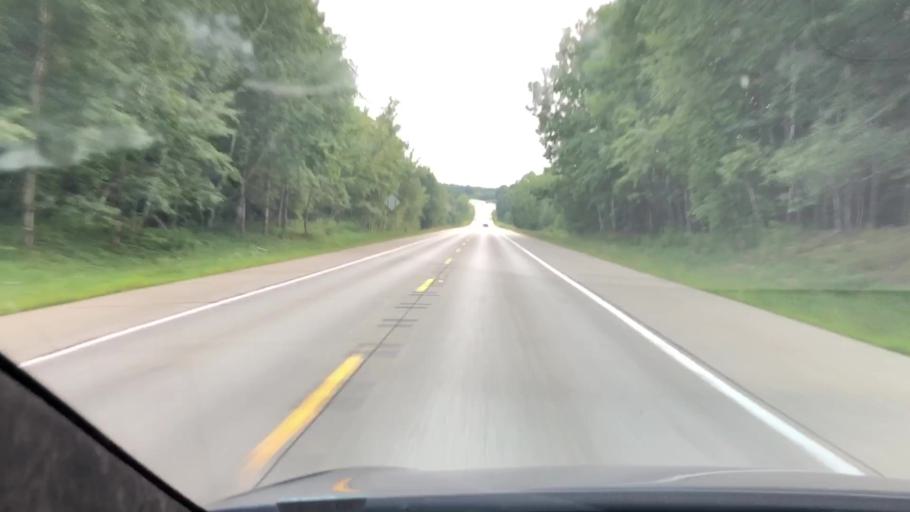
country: US
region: Pennsylvania
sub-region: Mercer County
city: Grove City
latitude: 41.2219
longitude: -79.9640
